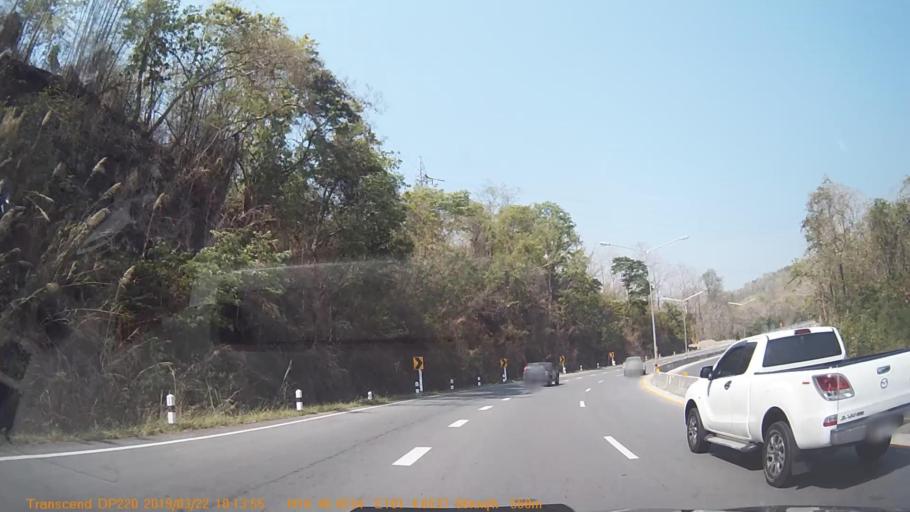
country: TH
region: Phetchabun
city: Khao Kho
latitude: 16.7735
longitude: 101.0771
